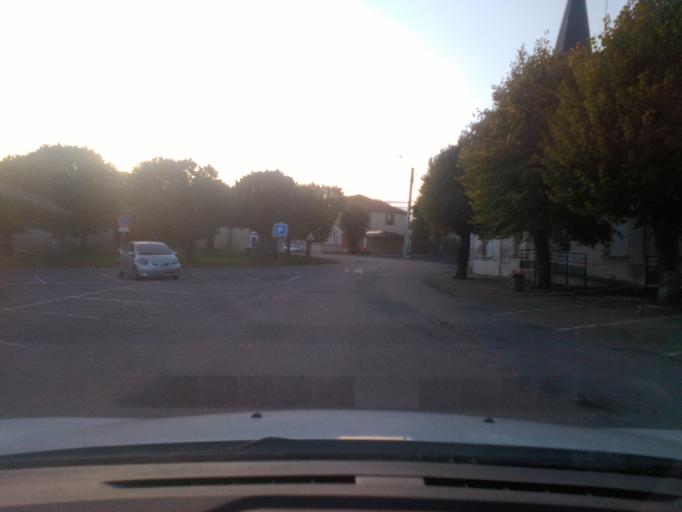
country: FR
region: Lorraine
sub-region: Departement des Vosges
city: Mirecourt
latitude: 48.3947
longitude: 6.1322
